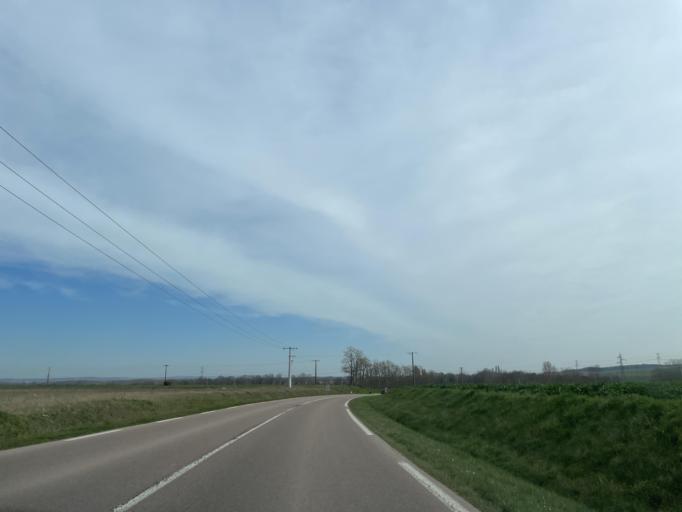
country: FR
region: Champagne-Ardenne
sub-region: Departement de l'Aube
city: Nogent-sur-Seine
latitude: 48.4935
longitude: 3.5234
